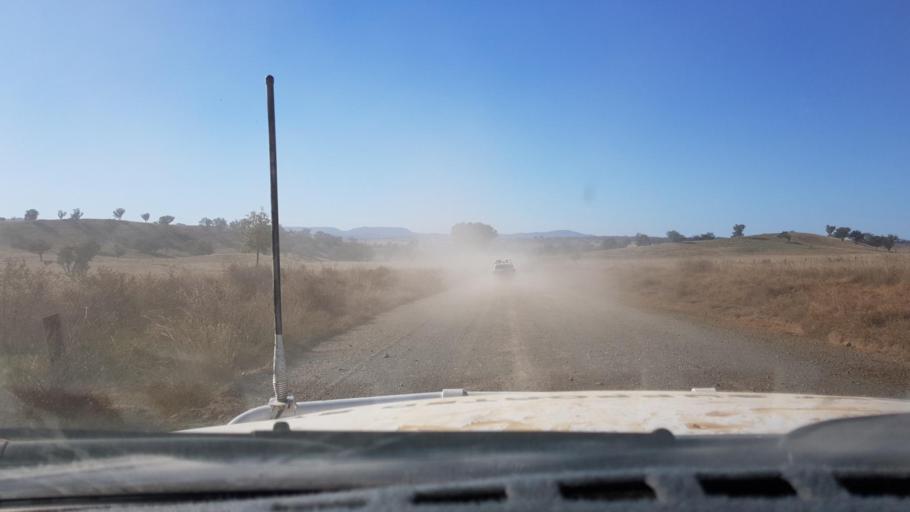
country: AU
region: New South Wales
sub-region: Narrabri
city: Blair Athol
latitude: -30.6741
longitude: 150.4099
